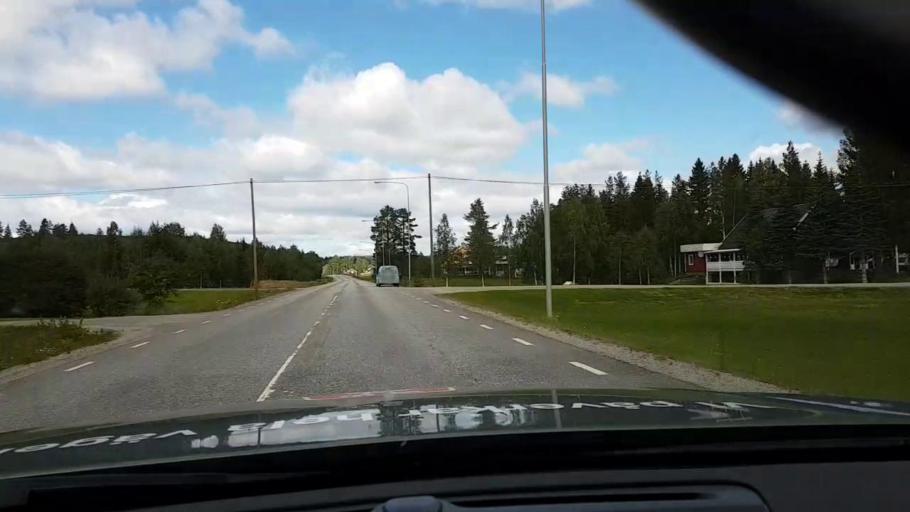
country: SE
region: Vaesternorrland
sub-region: OErnskoeldsviks Kommun
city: Bredbyn
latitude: 63.4765
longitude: 18.0947
